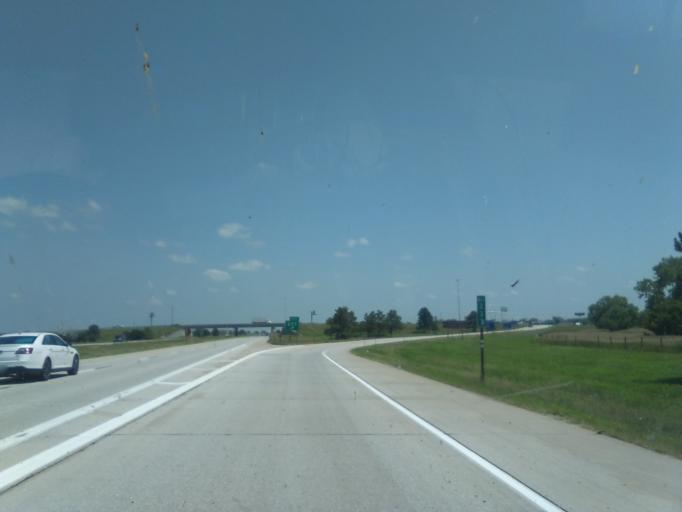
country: US
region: Nebraska
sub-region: Dawson County
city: Lexington
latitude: 40.7427
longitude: -99.7454
